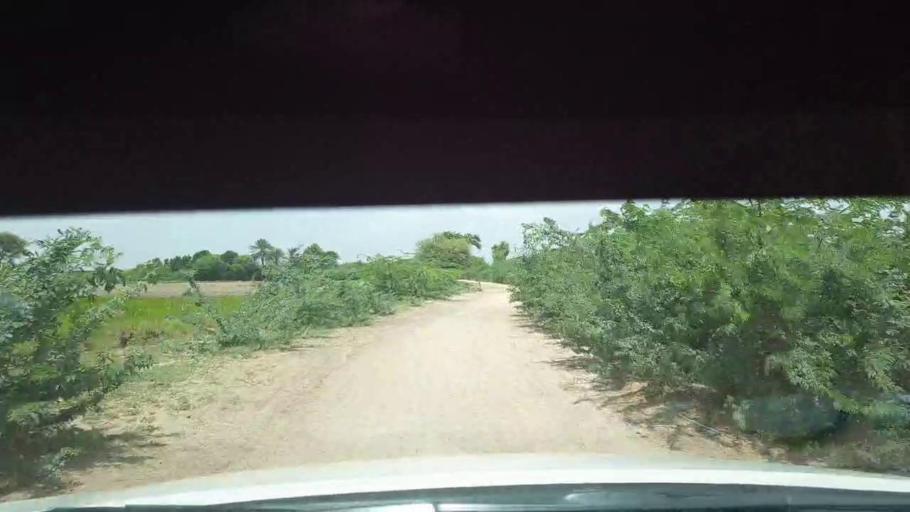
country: PK
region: Sindh
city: Kadhan
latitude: 24.5470
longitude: 68.9699
